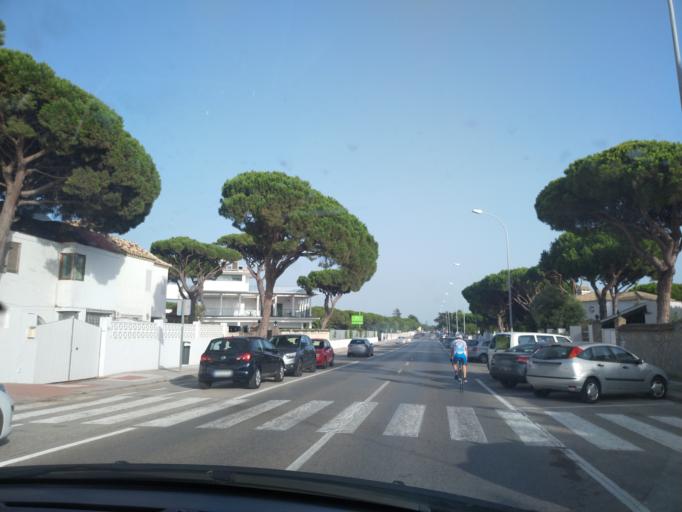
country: ES
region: Andalusia
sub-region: Provincia de Cadiz
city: Chiclana de la Frontera
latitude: 36.3749
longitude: -6.1850
